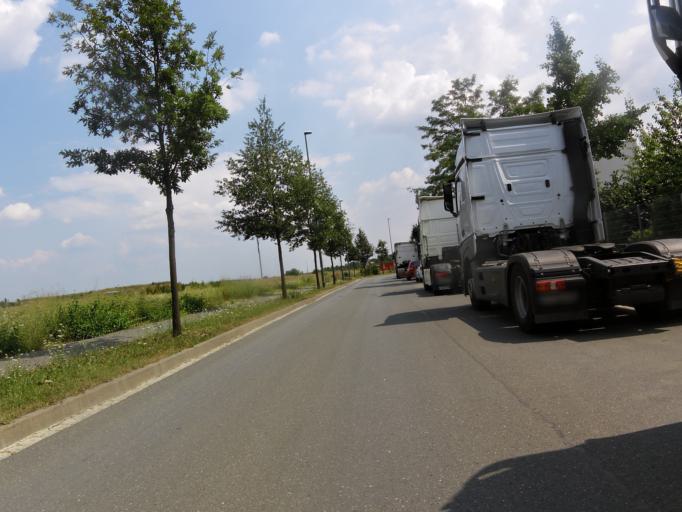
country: DE
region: Bavaria
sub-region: Regierungsbezirk Unterfranken
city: Randersacker
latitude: 49.7340
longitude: 9.9714
